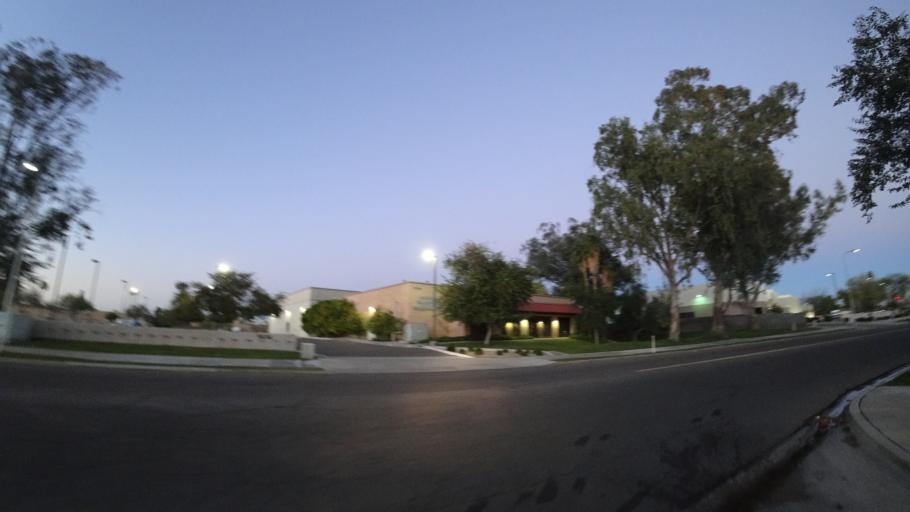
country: US
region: Arizona
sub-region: Maricopa County
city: Tempe Junction
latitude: 33.4135
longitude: -111.9631
